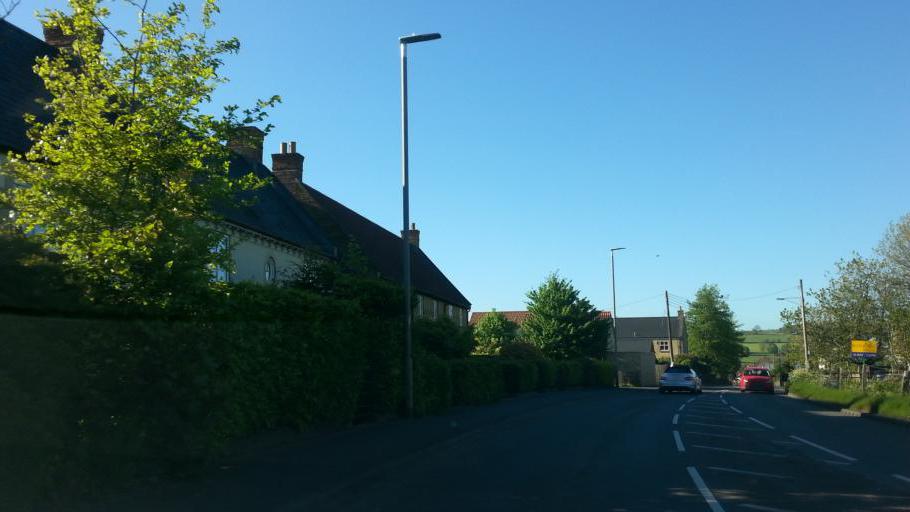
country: GB
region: England
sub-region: Somerset
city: Shepton Mallet
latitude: 51.1813
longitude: -2.5362
